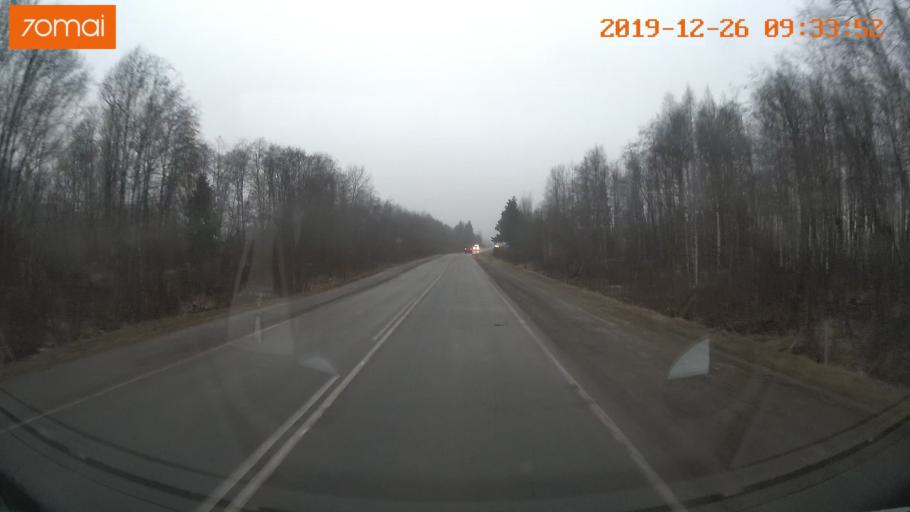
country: RU
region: Vologda
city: Vologda
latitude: 59.0948
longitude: 40.0940
